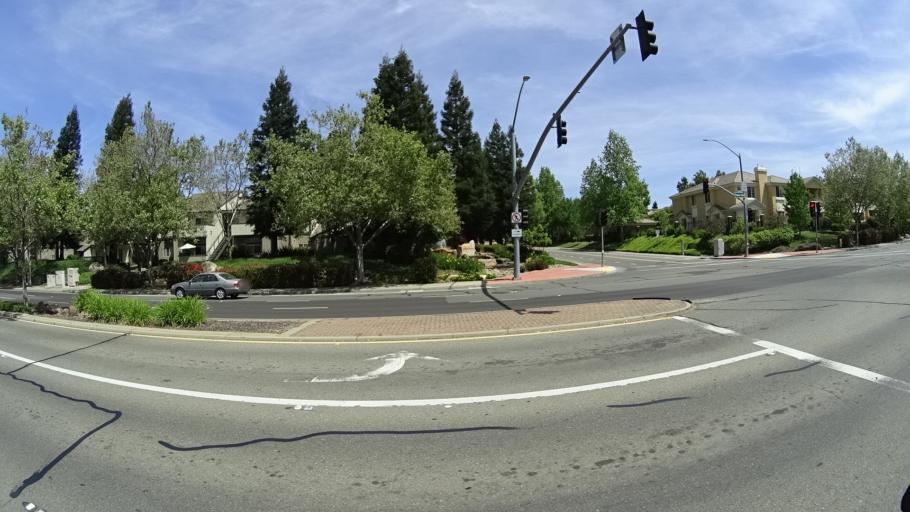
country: US
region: California
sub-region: Placer County
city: Rocklin
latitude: 38.8013
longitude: -121.2702
